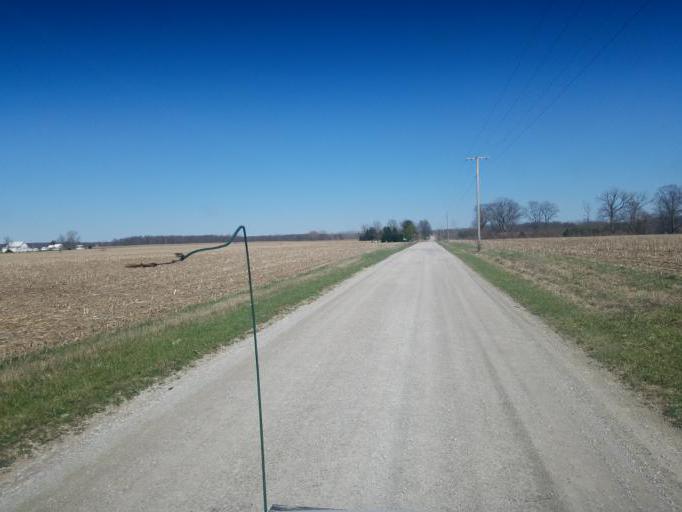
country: US
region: Ohio
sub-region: Morrow County
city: Mount Gilead
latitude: 40.5867
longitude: -82.9029
